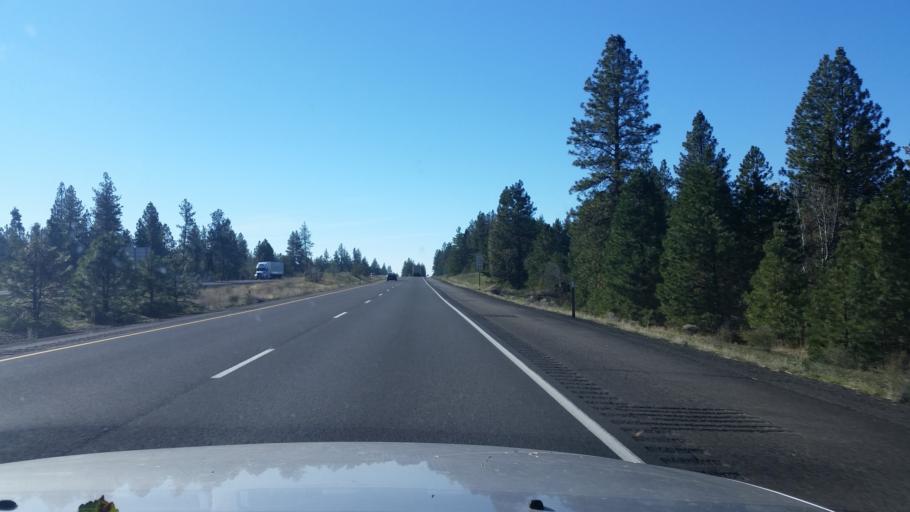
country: US
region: Washington
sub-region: Spokane County
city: Medical Lake
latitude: 47.4312
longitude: -117.7971
